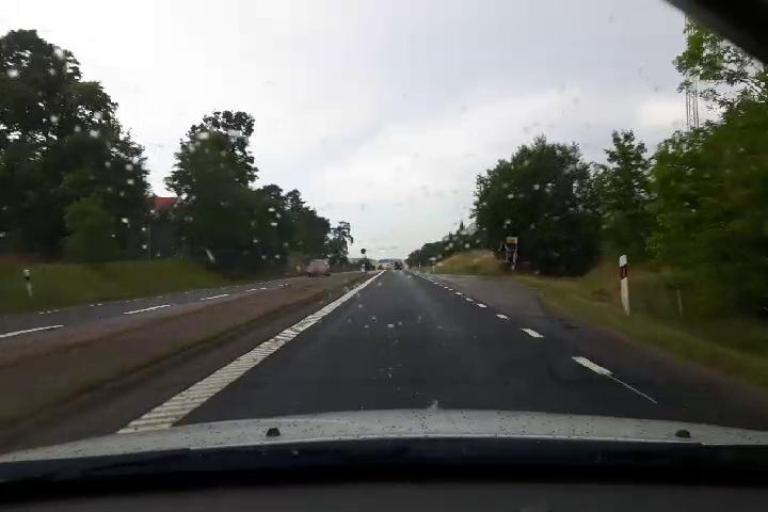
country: SE
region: Uppsala
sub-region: Uppsala Kommun
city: Gamla Uppsala
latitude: 59.9586
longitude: 17.5844
